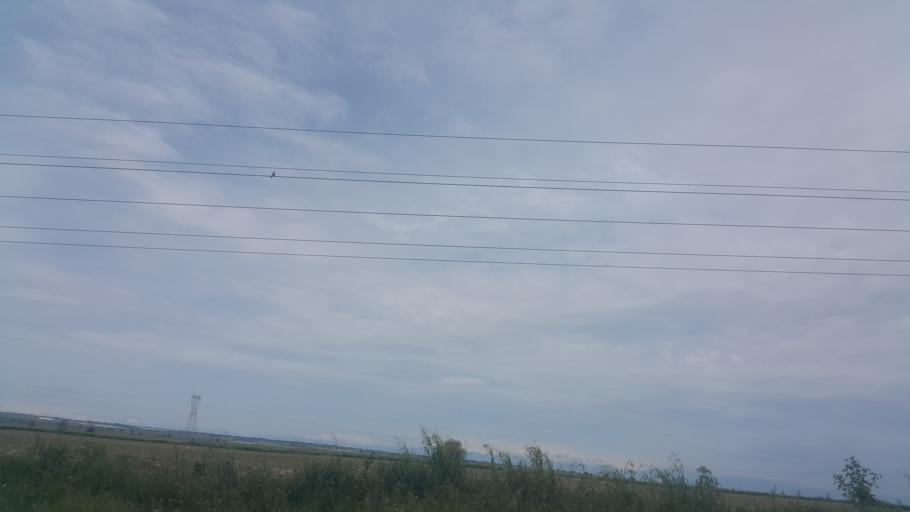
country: TR
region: Adana
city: Ceyhan
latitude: 37.0189
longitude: 35.7189
